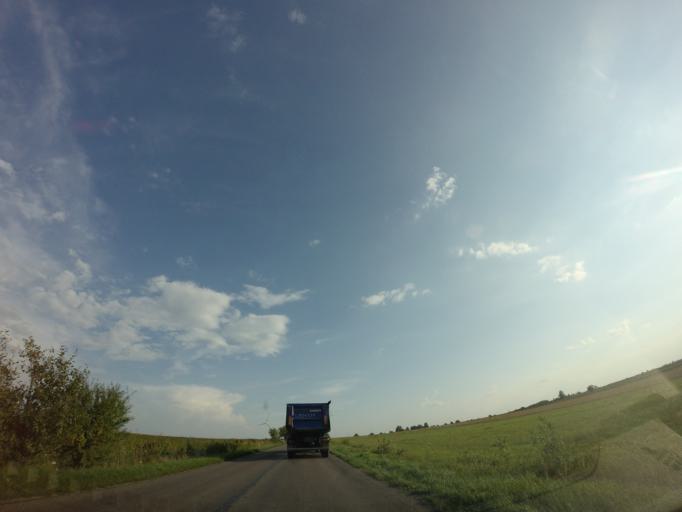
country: PL
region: Lublin Voivodeship
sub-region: Powiat lubartowski
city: Michow
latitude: 51.5007
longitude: 22.3068
